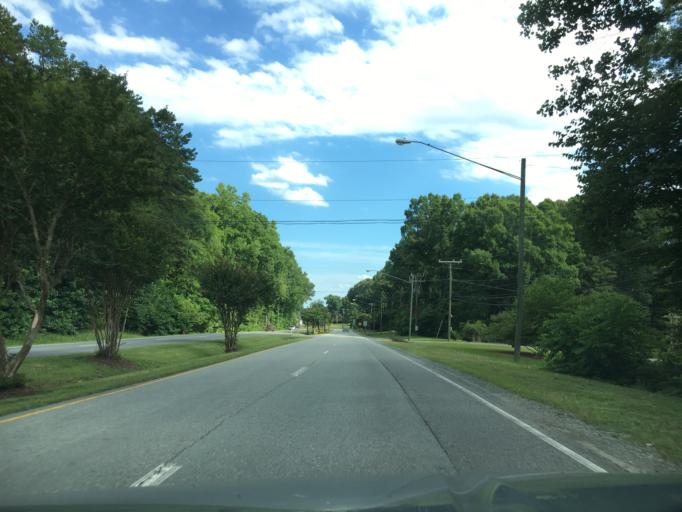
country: US
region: Virginia
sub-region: Halifax County
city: South Boston
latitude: 36.7188
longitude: -78.9174
